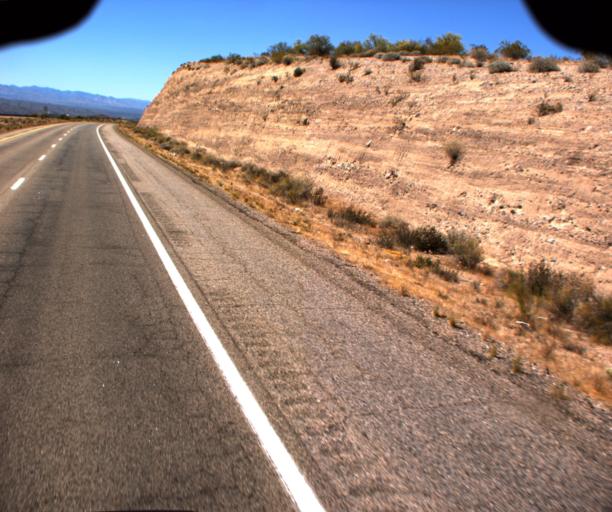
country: US
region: Arizona
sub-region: Yavapai County
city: Bagdad
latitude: 34.5926
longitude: -113.5131
